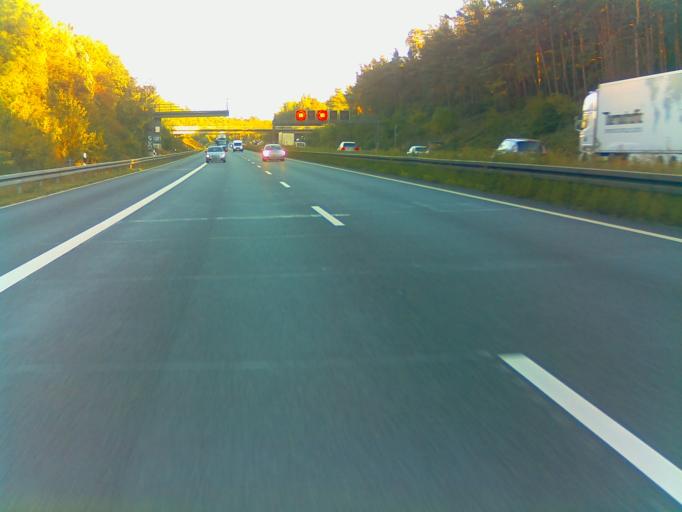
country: DE
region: Hesse
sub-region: Regierungsbezirk Darmstadt
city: Darmstadt
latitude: 49.8457
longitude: 8.6172
